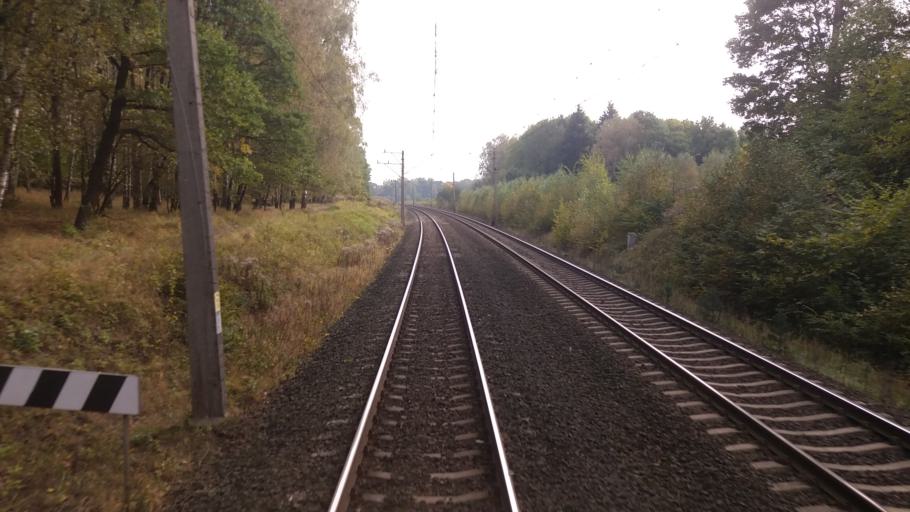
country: PL
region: West Pomeranian Voivodeship
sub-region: Powiat stargardzki
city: Dolice
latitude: 53.1703
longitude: 15.2917
